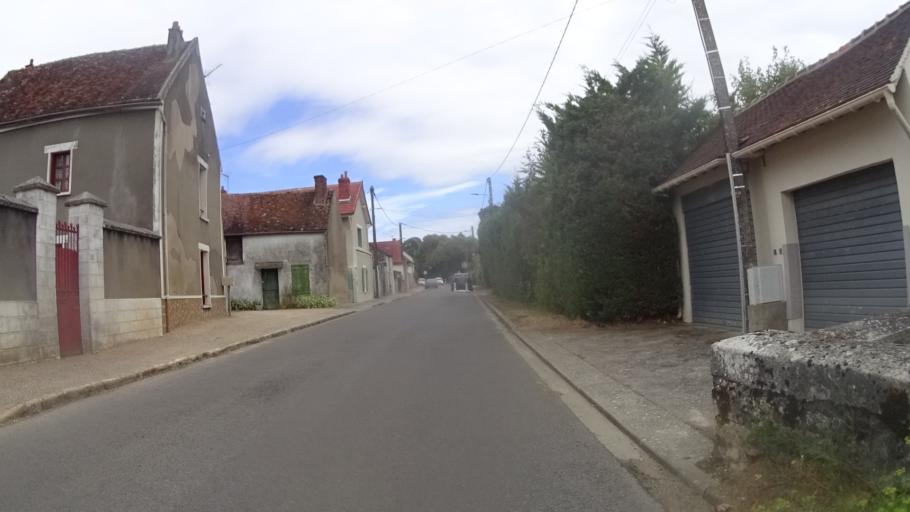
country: FR
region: Centre
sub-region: Departement du Loiret
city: Malesherbes
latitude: 48.2337
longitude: 2.4289
